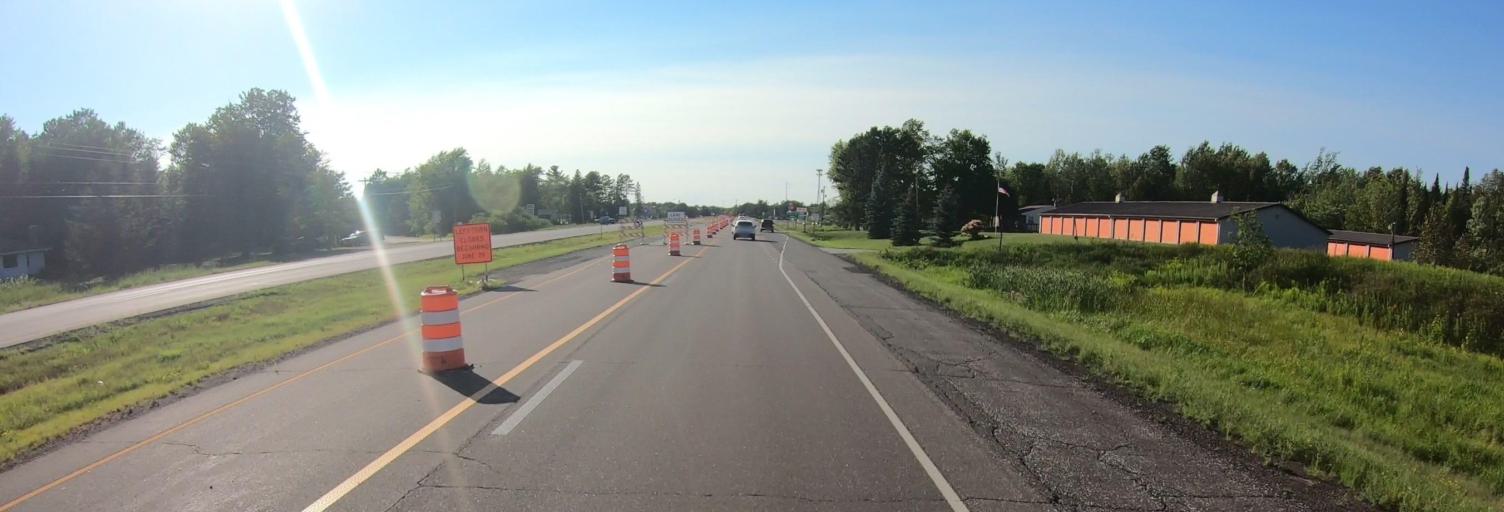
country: US
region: Minnesota
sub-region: Saint Louis County
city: Hermantown
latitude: 46.8486
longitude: -92.2748
